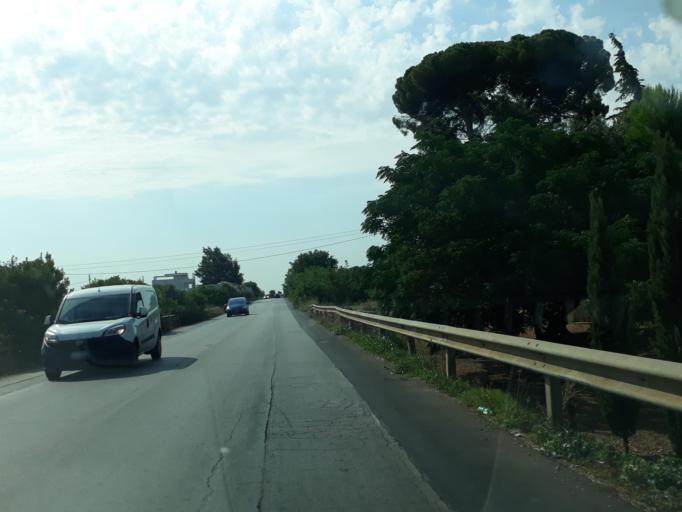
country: IT
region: Apulia
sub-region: Provincia di Brindisi
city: Carovigno
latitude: 40.6977
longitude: 17.6666
